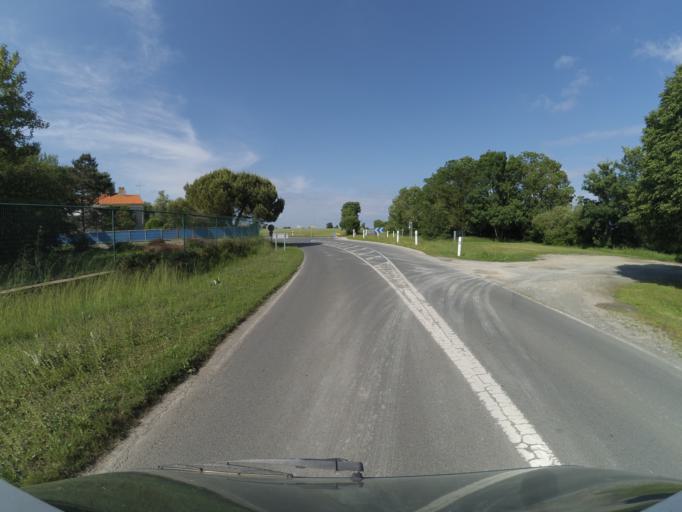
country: FR
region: Poitou-Charentes
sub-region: Departement de la Charente-Maritime
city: Andilly
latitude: 46.2467
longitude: -1.0614
